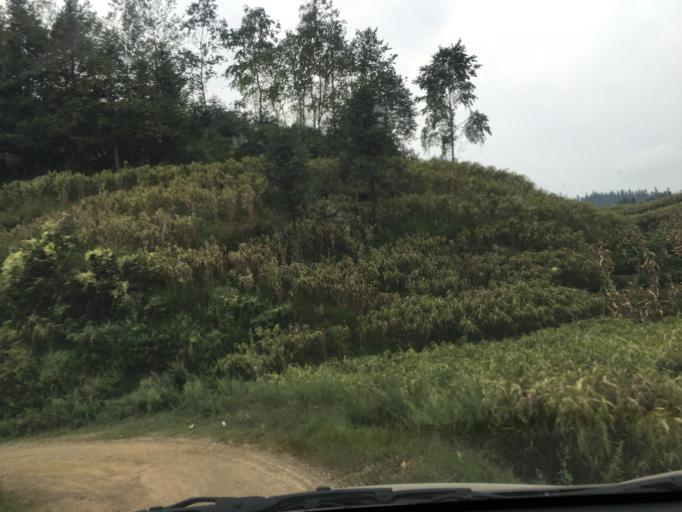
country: CN
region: Guangxi Zhuangzu Zizhiqu
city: Xinzhou
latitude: 25.5399
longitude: 105.5298
